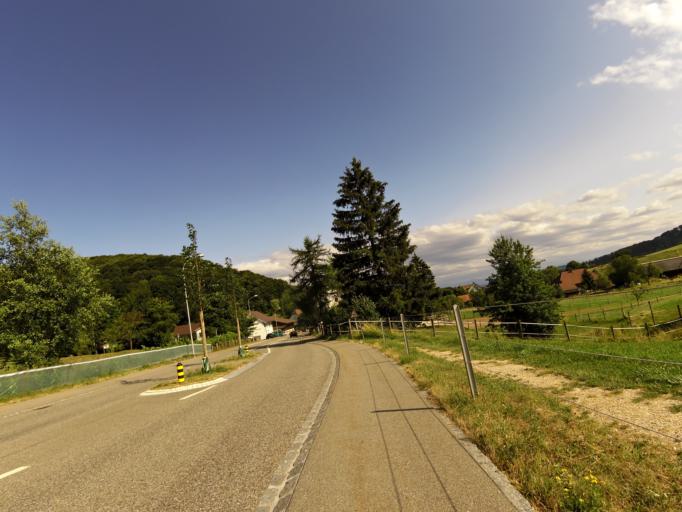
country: CH
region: Basel-Landschaft
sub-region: Bezirk Sissach
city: Laufelfingen
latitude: 47.3802
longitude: 7.8703
